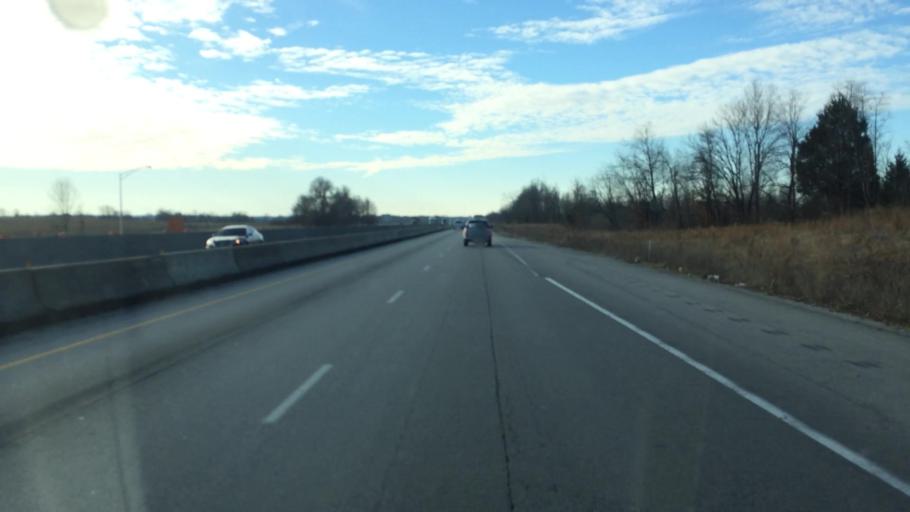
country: US
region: Kentucky
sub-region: Hardin County
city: Elizabethtown
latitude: 37.5915
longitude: -85.8699
